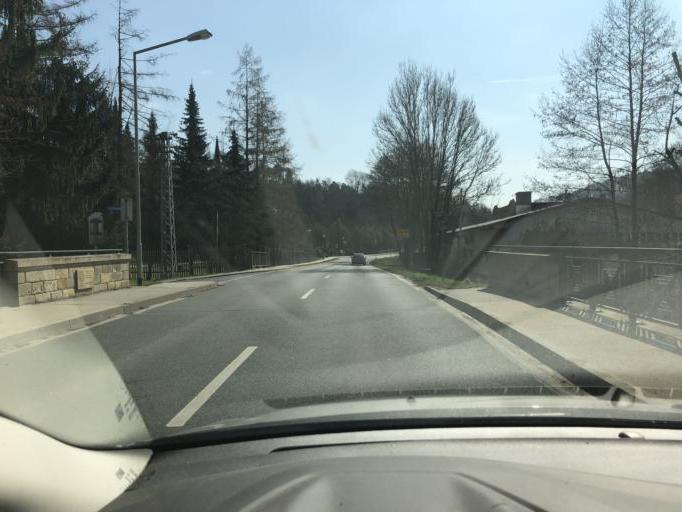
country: DE
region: Thuringia
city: Rudolstadt
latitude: 50.7350
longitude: 11.3325
